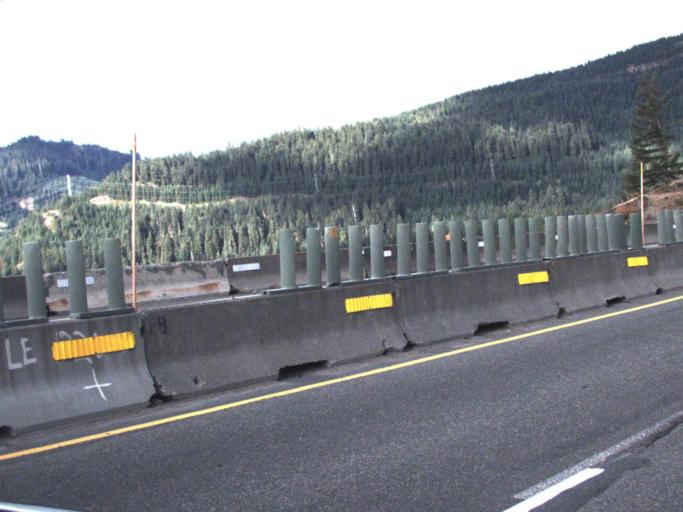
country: US
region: Washington
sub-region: King County
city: Tanner
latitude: 47.3409
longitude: -121.3608
